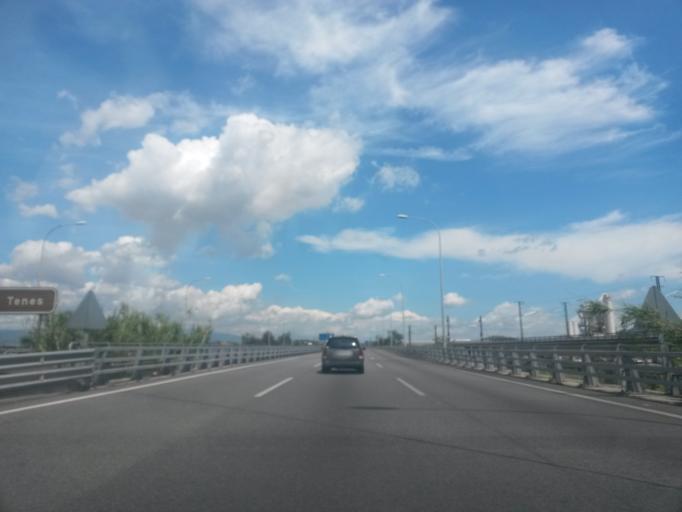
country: ES
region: Catalonia
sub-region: Provincia de Barcelona
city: Montmelo
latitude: 41.5427
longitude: 2.2297
